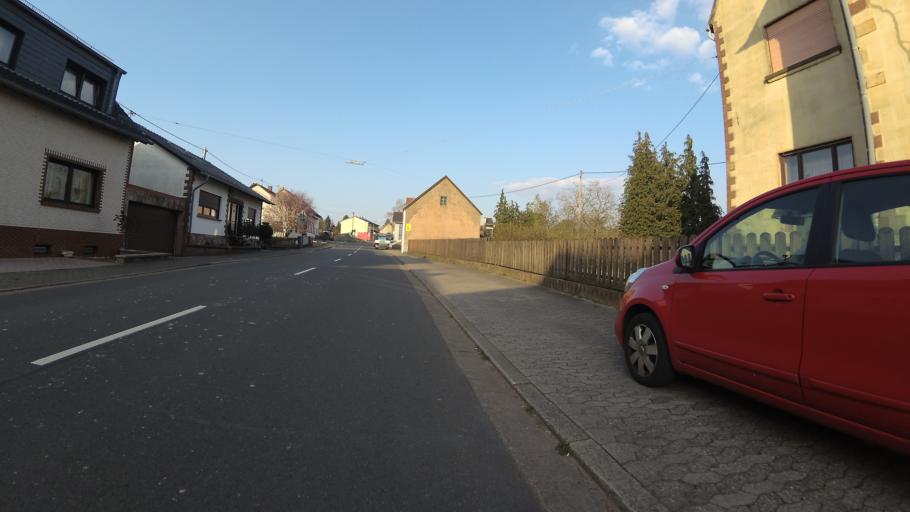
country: DE
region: Saarland
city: Merchweiler
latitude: 49.3450
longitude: 7.0004
